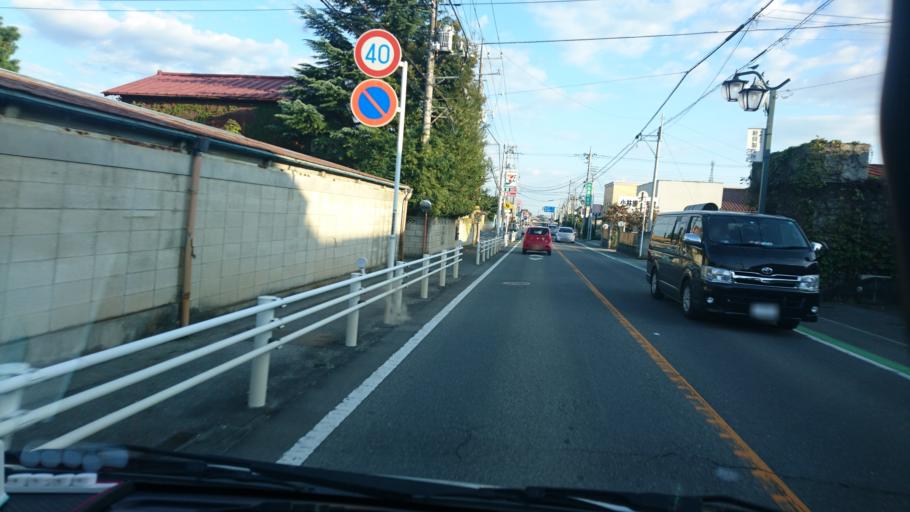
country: JP
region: Gunma
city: Kiryu
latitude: 36.4095
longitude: 139.3118
